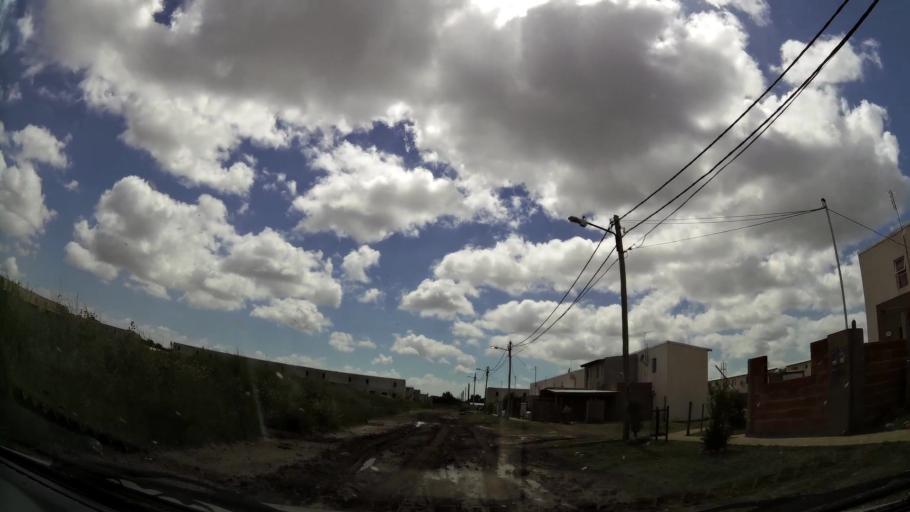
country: AR
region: Buenos Aires
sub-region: Partido de Quilmes
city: Quilmes
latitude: -34.8296
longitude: -58.2113
